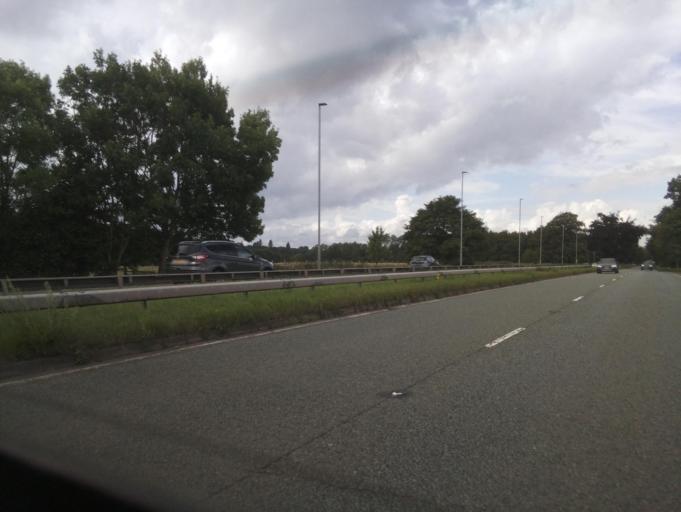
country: GB
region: England
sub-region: Staffordshire
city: Barlaston
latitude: 52.9554
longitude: -2.1926
